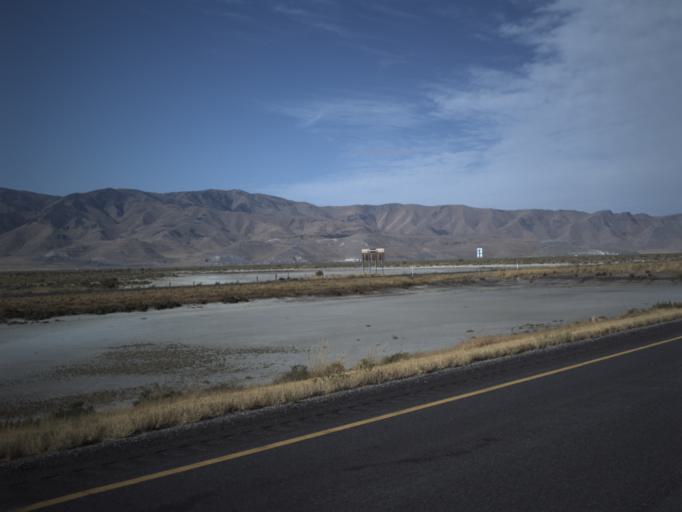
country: US
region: Utah
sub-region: Tooele County
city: Grantsville
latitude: 40.6922
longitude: -112.4649
